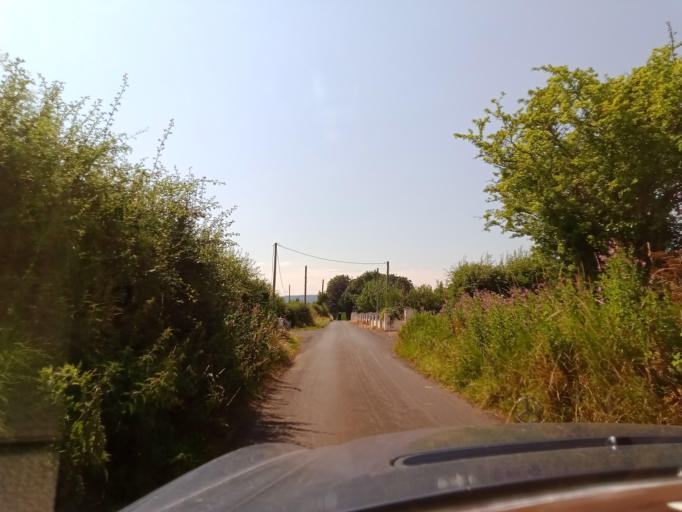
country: IE
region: Leinster
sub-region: Kilkenny
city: Mooncoin
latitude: 52.3109
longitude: -7.2829
